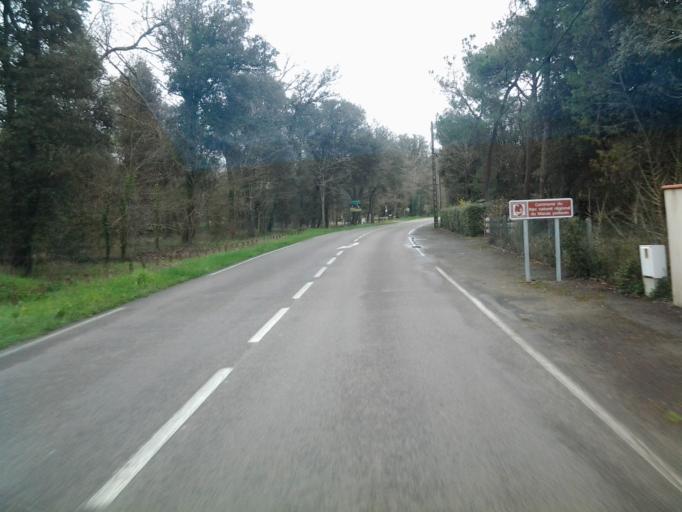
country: FR
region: Pays de la Loire
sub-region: Departement de la Vendee
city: Longeville-sur-Mer
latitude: 46.4048
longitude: -1.4893
